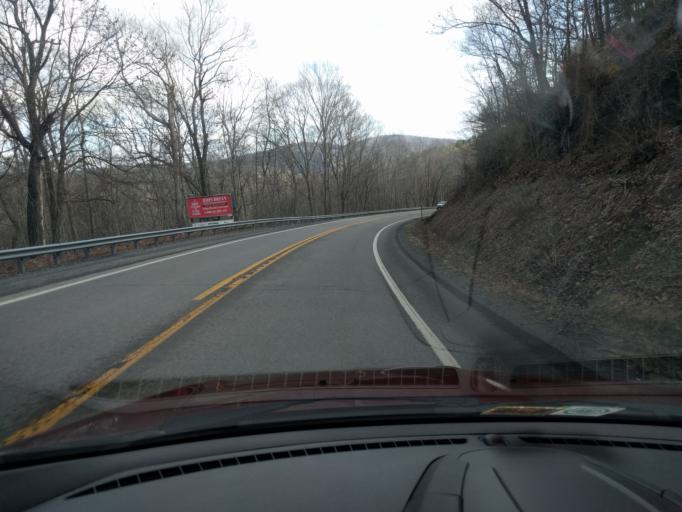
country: US
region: West Virginia
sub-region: Greenbrier County
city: Lewisburg
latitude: 37.7941
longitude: -80.4191
